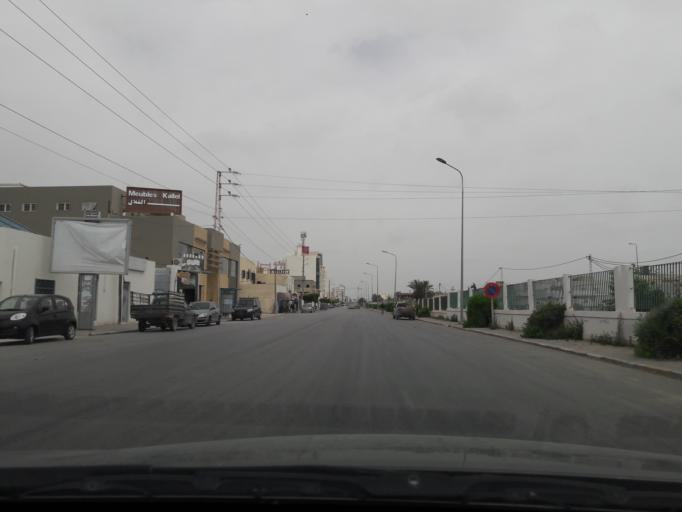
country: TN
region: Safaqis
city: Al Qarmadah
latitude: 34.7750
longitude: 10.7611
